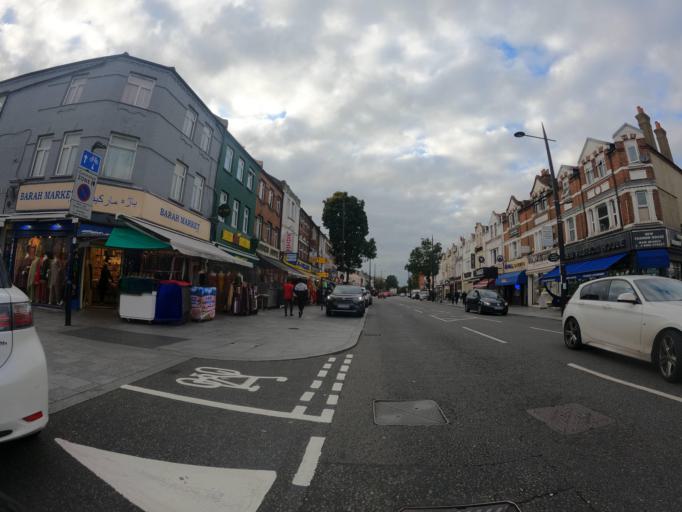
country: GB
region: England
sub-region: Greater London
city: Southall
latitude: 51.5115
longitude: -0.3801
